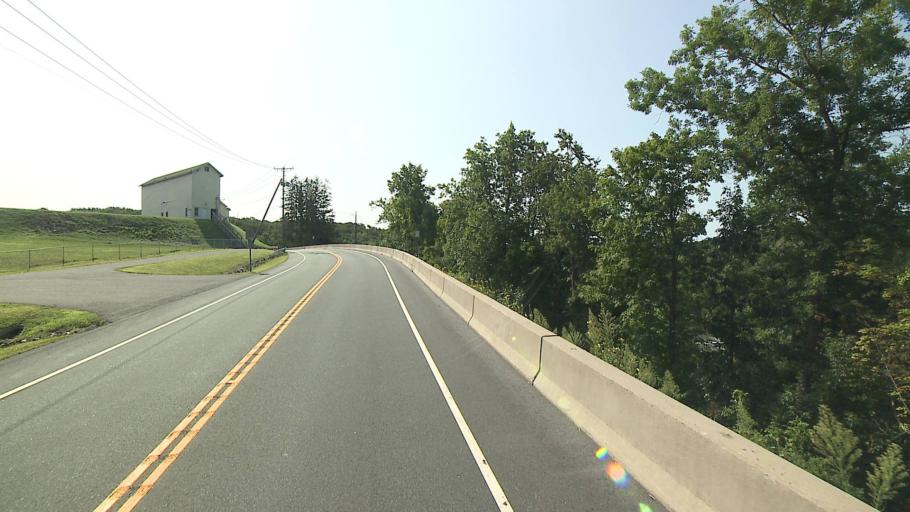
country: US
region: Connecticut
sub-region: Litchfield County
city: Kent
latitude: 41.6607
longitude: -73.4927
